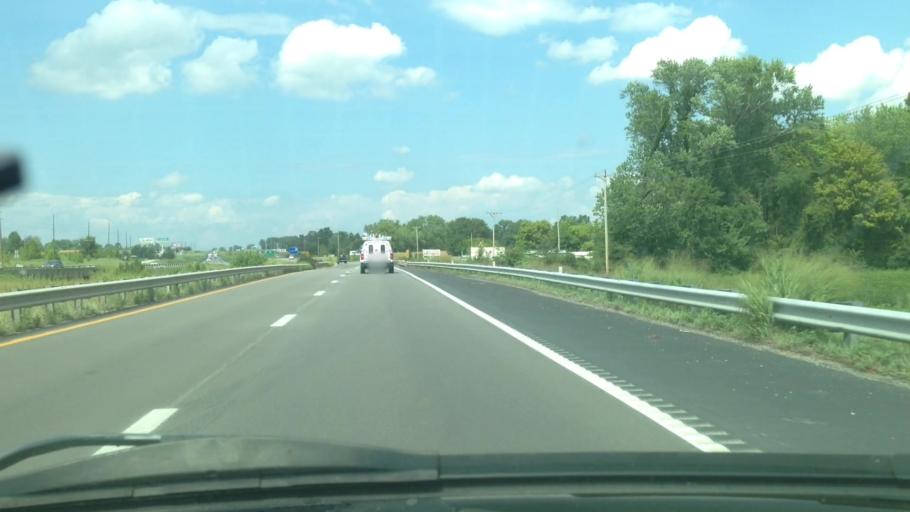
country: US
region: Missouri
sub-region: Lincoln County
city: Moscow Mills
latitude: 38.9262
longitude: -90.9248
